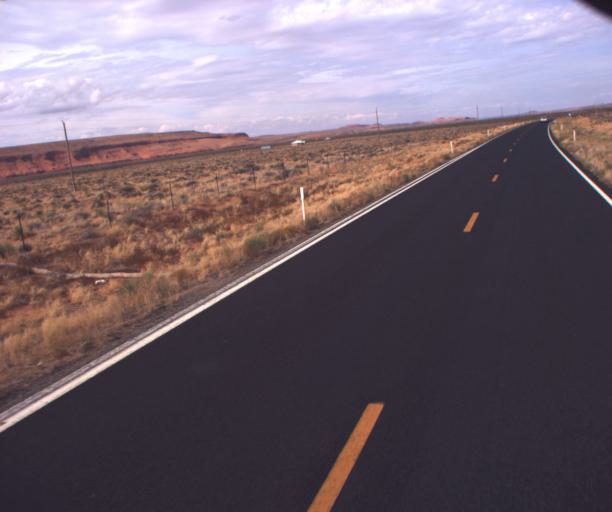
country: US
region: Arizona
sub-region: Apache County
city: Many Farms
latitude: 36.6154
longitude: -109.5795
